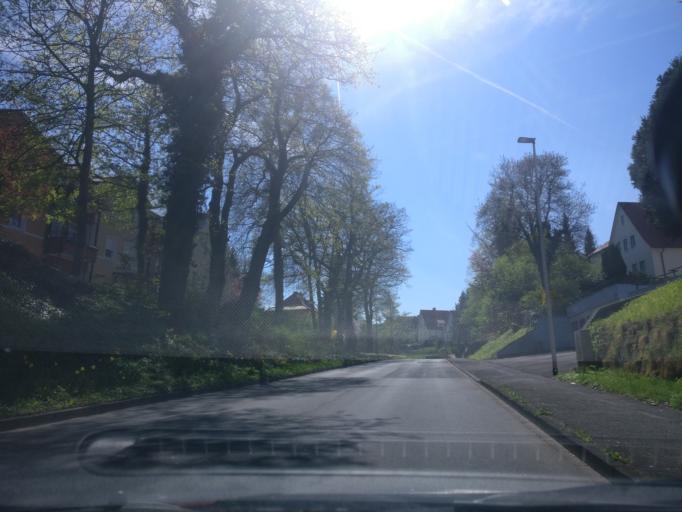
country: DE
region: Lower Saxony
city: Hannoversch Munden
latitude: 51.4097
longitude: 9.6543
